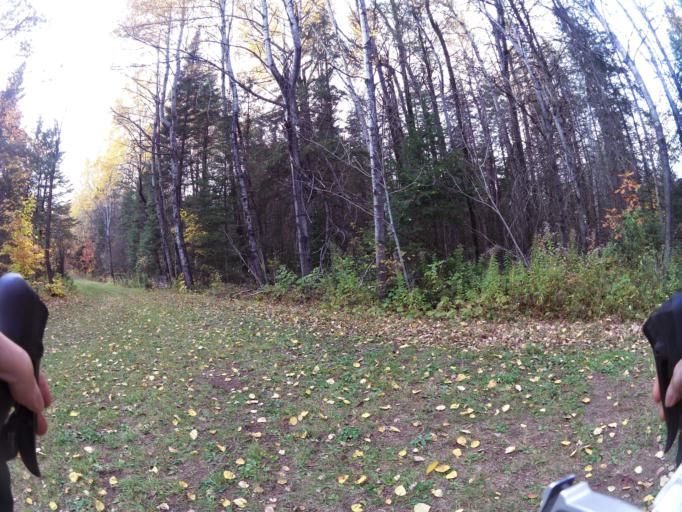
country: CA
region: Quebec
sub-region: Outaouais
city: Wakefield
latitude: 45.6171
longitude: -76.0270
